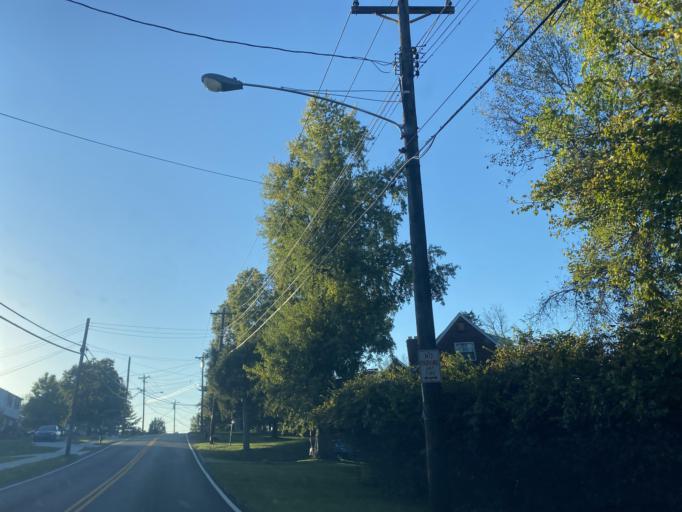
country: US
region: Kentucky
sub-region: Campbell County
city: Dayton
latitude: 39.1060
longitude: -84.4549
